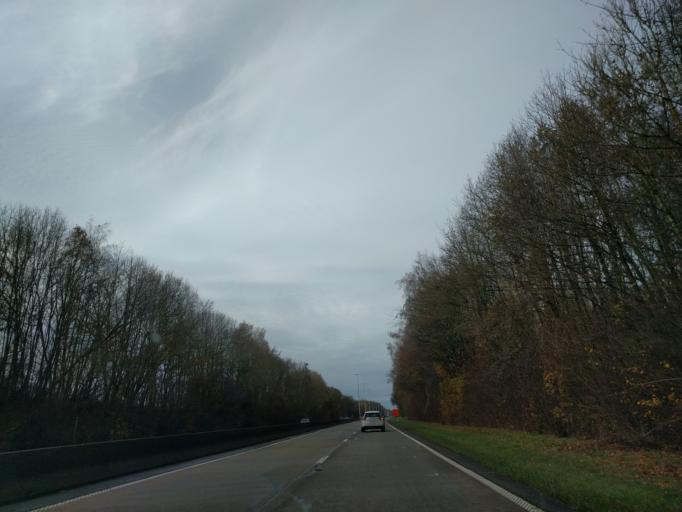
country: BE
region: Wallonia
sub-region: Province de Namur
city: Houyet
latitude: 50.2405
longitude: 4.9763
